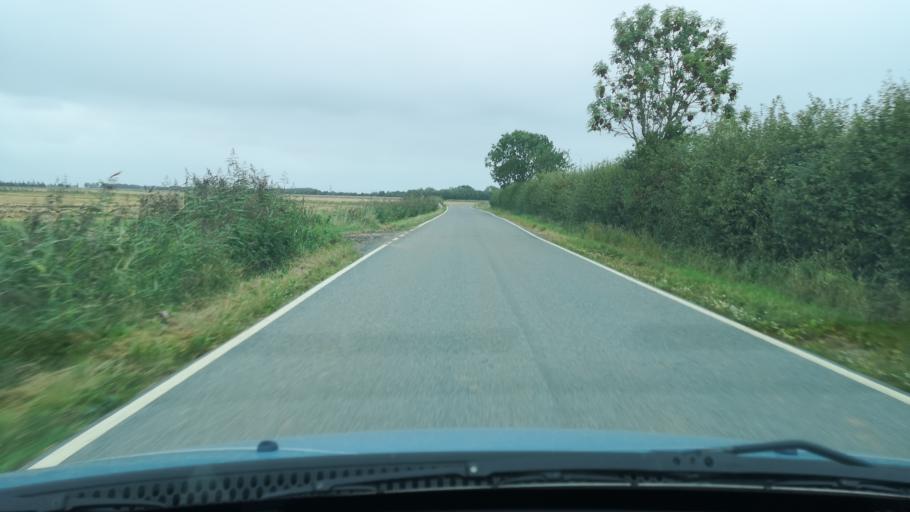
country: GB
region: England
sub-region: North Lincolnshire
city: Burton upon Stather
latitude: 53.6926
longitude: -0.7239
